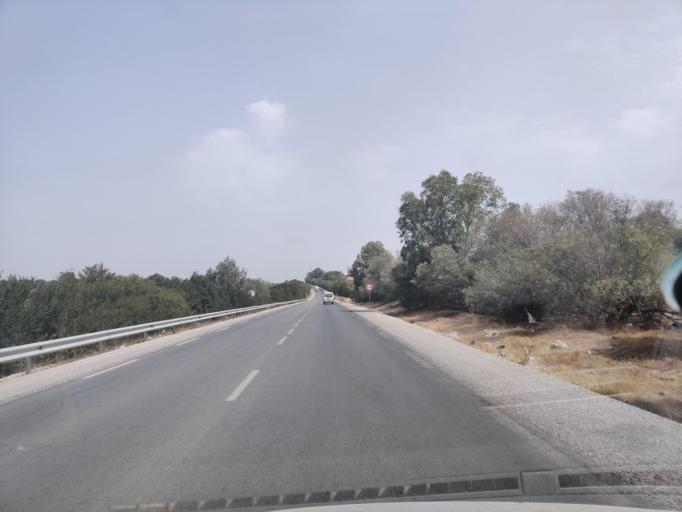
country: TN
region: Nabul
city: Bu `Urqub
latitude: 36.4728
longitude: 10.5722
